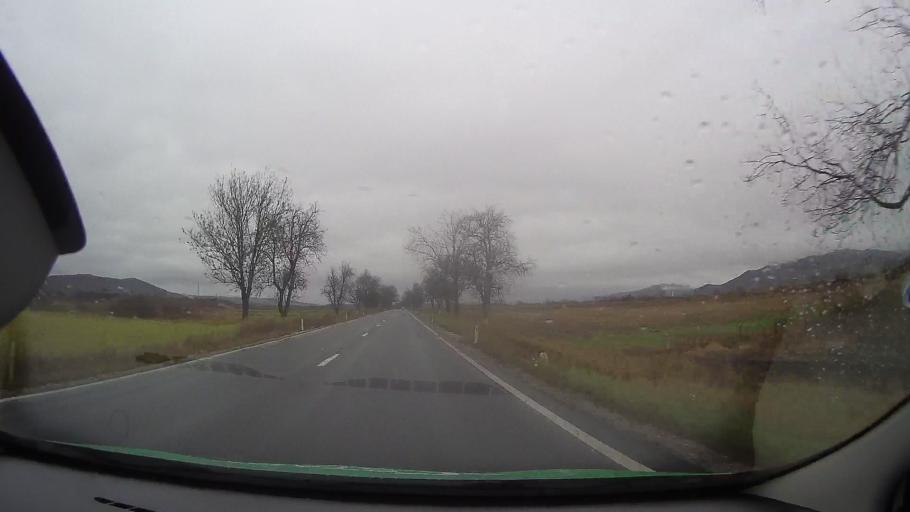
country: RO
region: Mures
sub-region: Comuna Suseni
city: Suseni
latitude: 46.8270
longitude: 24.7395
